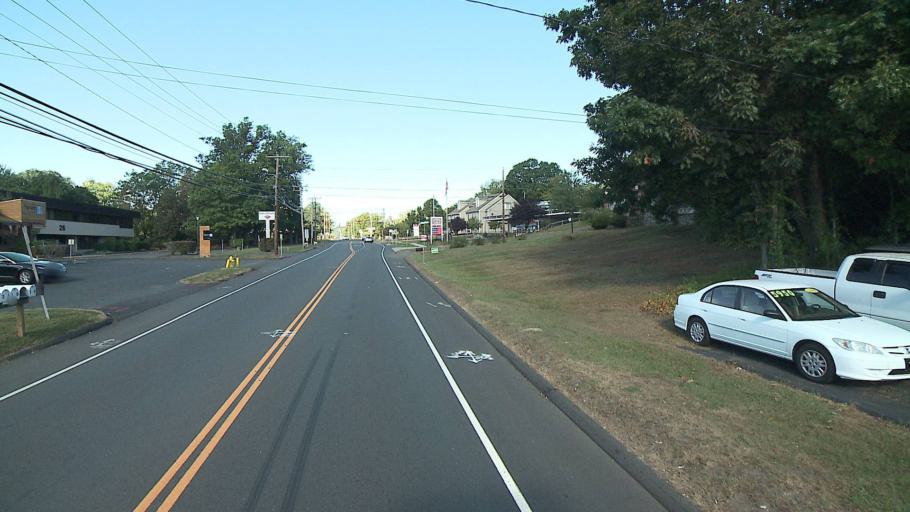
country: US
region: Connecticut
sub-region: Fairfield County
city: Danbury
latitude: 41.3882
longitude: -73.4954
